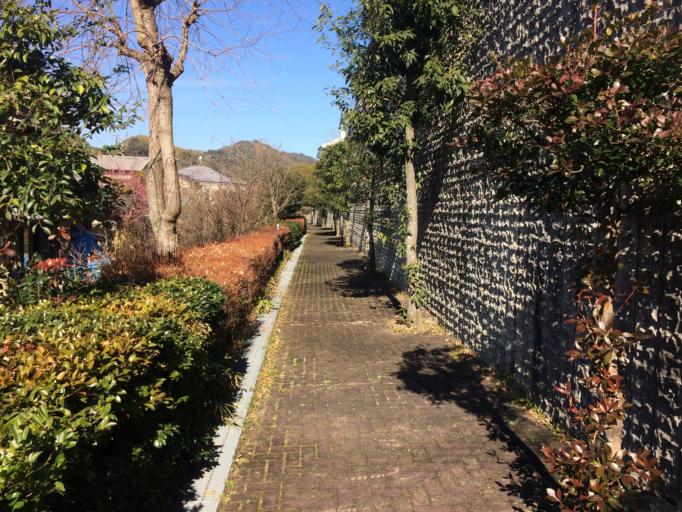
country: JP
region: Shizuoka
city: Shizuoka-shi
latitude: 35.0553
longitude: 138.4852
